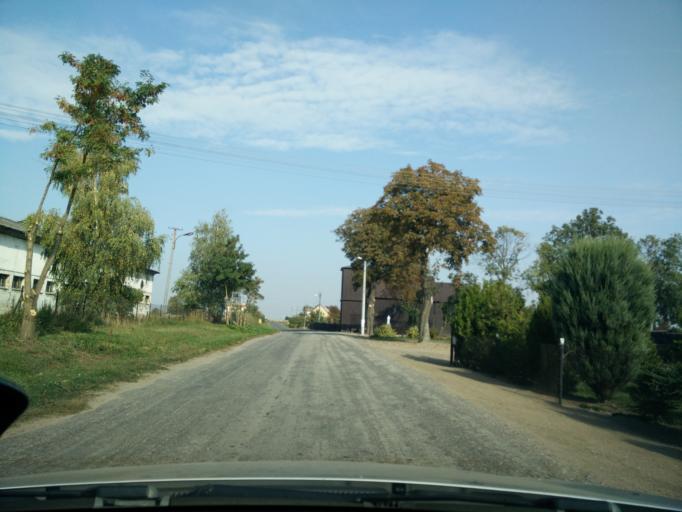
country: PL
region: Greater Poland Voivodeship
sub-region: Powiat sredzki
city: Dominowo
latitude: 52.2875
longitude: 17.3163
